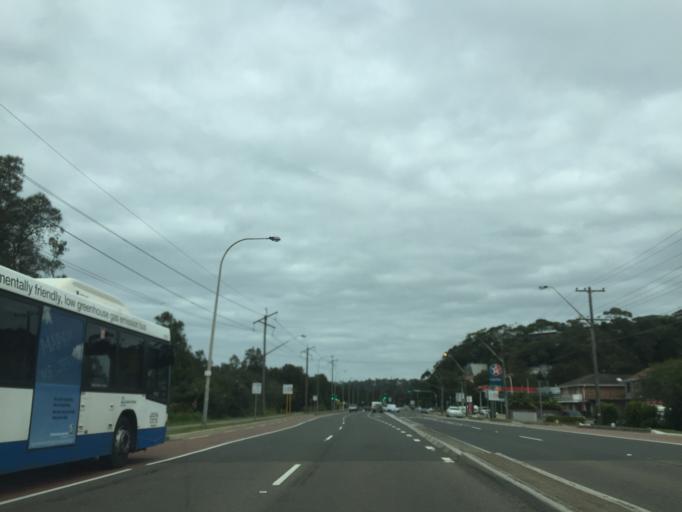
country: AU
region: New South Wales
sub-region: Pittwater
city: North Narrabeen
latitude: -33.7036
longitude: 151.2976
